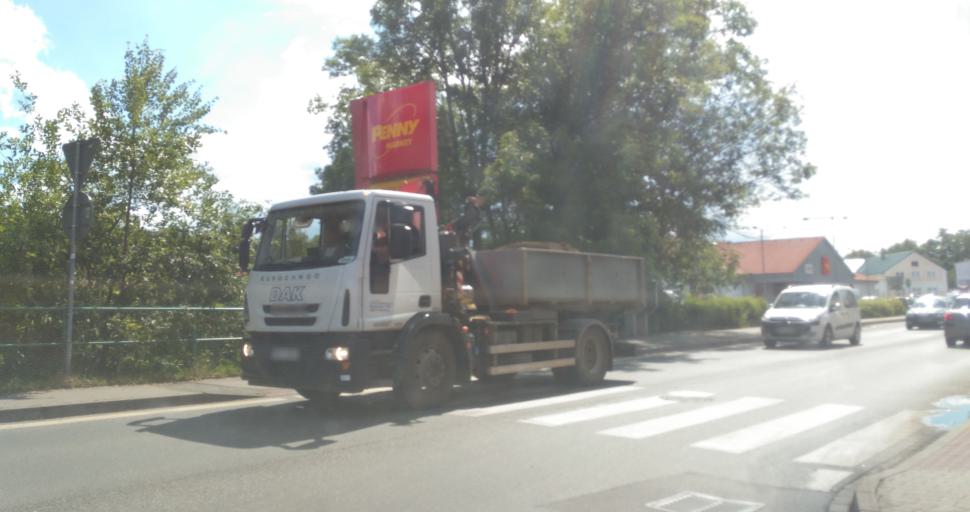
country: CZ
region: Central Bohemia
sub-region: Okres Beroun
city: Horovice
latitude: 49.8377
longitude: 13.8975
